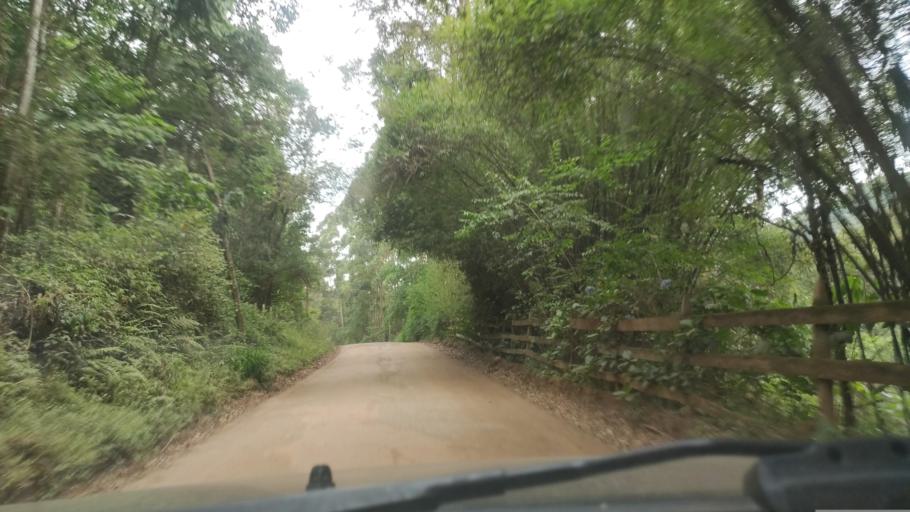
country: BR
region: Minas Gerais
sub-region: Paraisopolis
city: Paraisopolis
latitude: -22.6846
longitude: -45.8542
